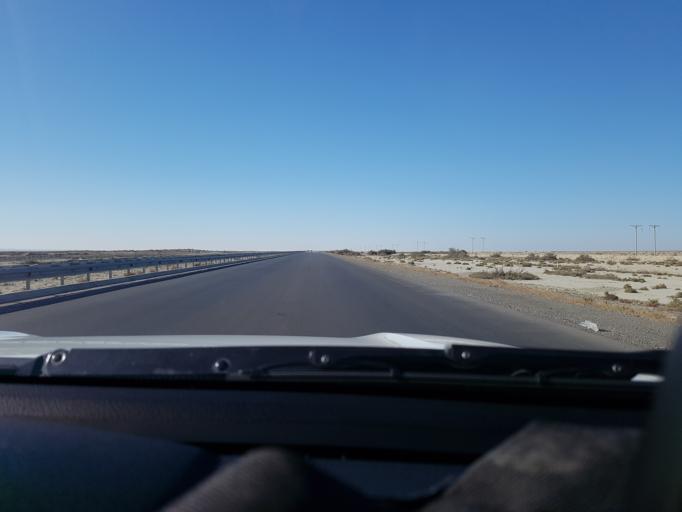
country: TM
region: Balkan
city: Gazanjyk
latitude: 39.2455
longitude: 55.0922
